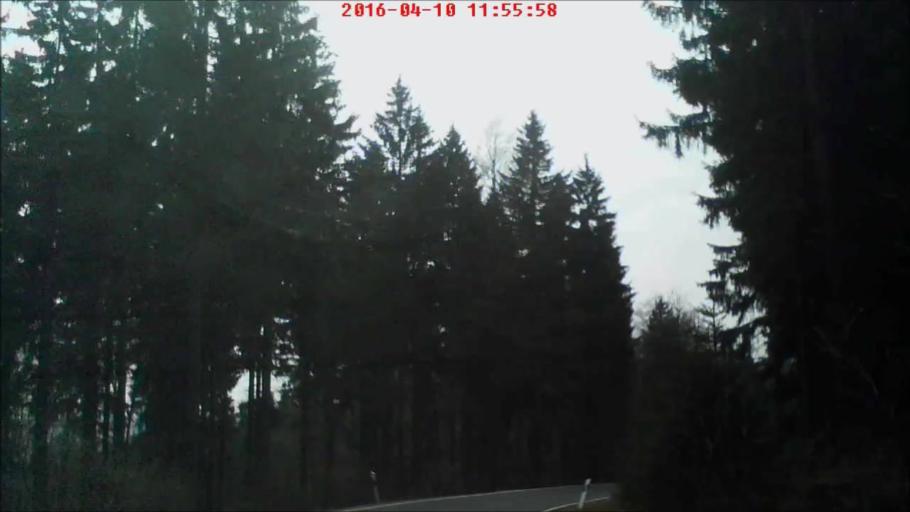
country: DE
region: Thuringia
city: Bermbach
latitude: 50.6852
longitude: 10.6457
